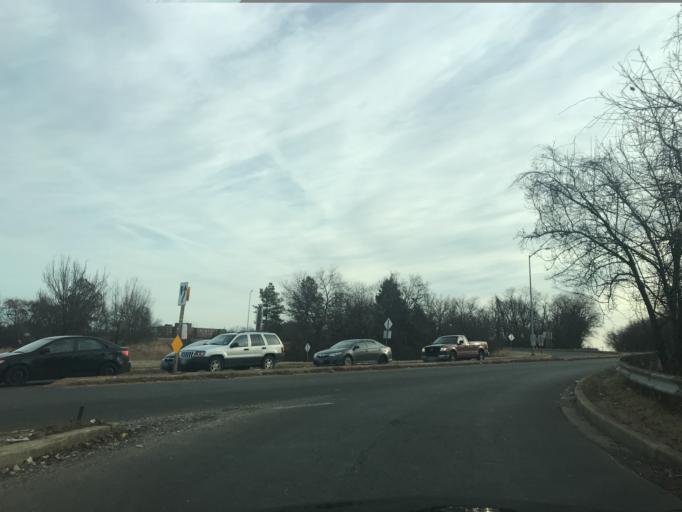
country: US
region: Maryland
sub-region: Prince George's County
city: Marlow Heights
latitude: 38.8310
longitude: -76.9409
